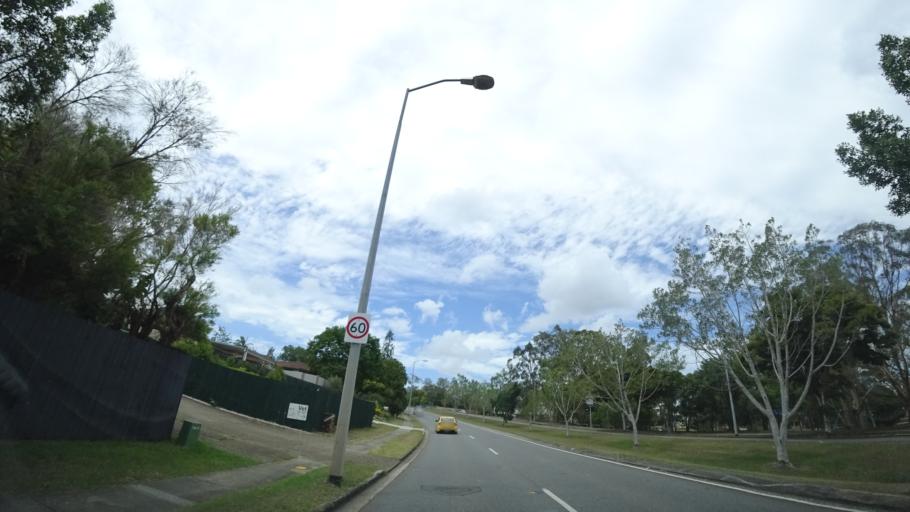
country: AU
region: Queensland
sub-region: Brisbane
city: Everton Park
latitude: -27.3832
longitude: 152.9871
